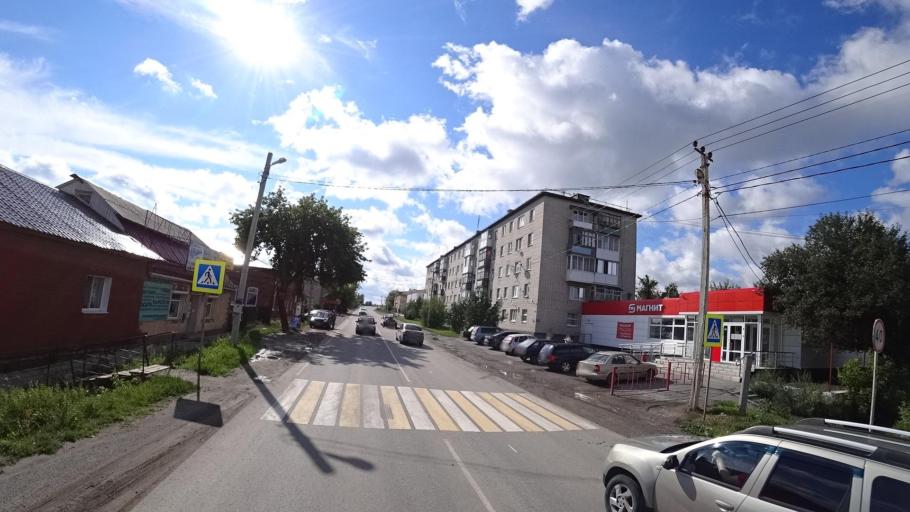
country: RU
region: Sverdlovsk
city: Kamyshlov
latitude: 56.8450
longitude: 62.6946
